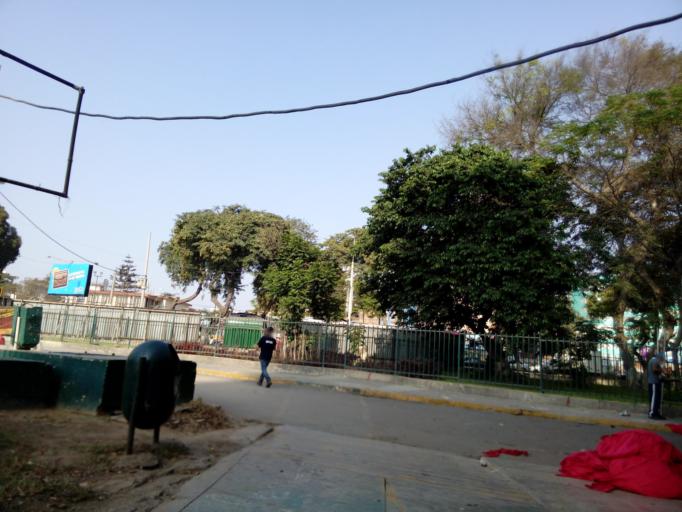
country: PE
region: Lima
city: Lima
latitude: -12.0655
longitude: -77.0396
